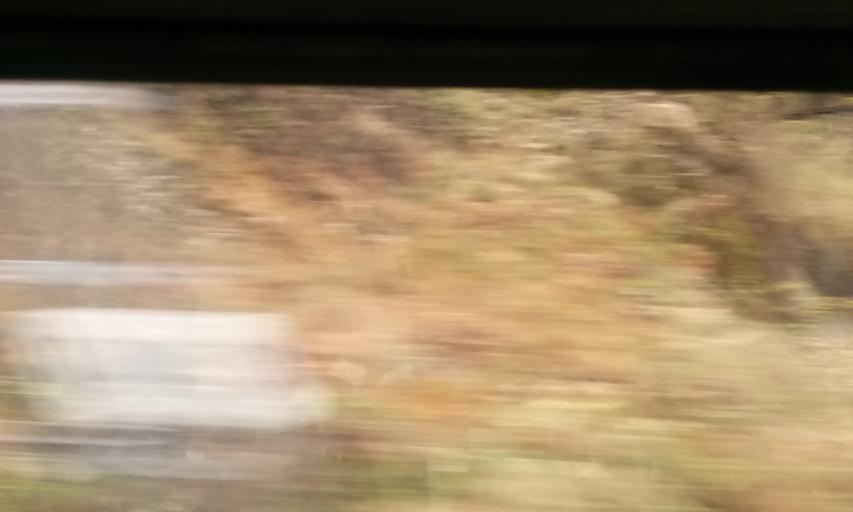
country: JP
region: Gifu
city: Nakatsugawa
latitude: 35.6113
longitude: 137.6114
